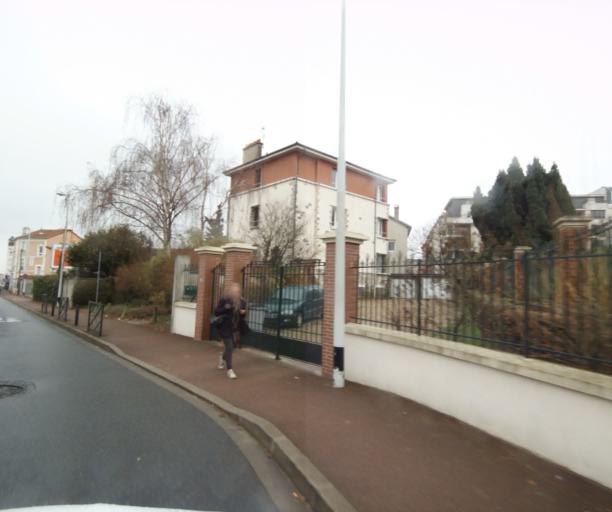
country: FR
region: Ile-de-France
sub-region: Departement des Hauts-de-Seine
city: Suresnes
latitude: 48.8795
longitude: 2.2173
